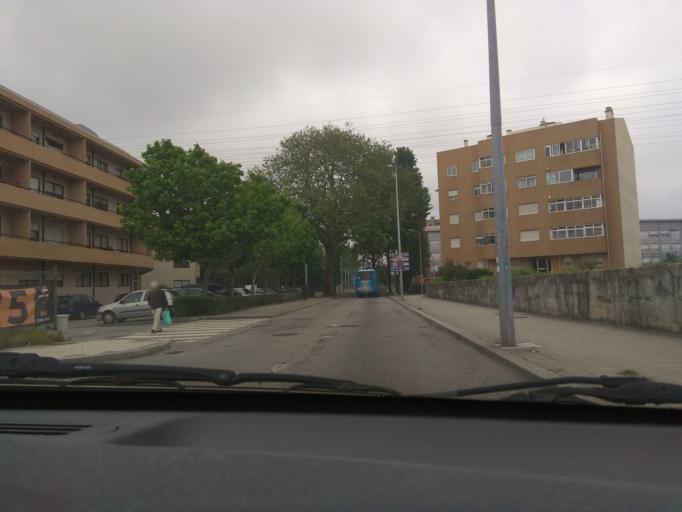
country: PT
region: Porto
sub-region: Matosinhos
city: Senhora da Hora
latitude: 41.1919
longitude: -8.6593
